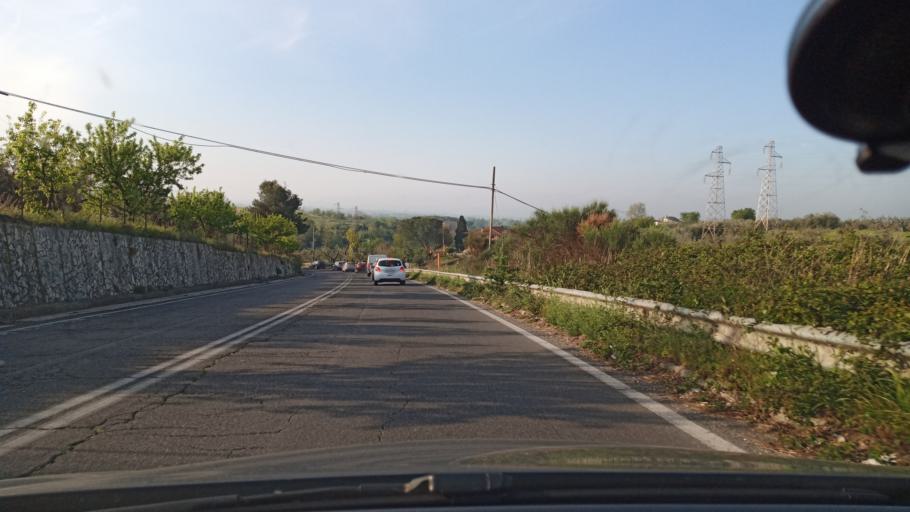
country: IT
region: Latium
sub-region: Citta metropolitana di Roma Capitale
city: Fiano Romano
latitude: 42.1799
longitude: 12.6358
